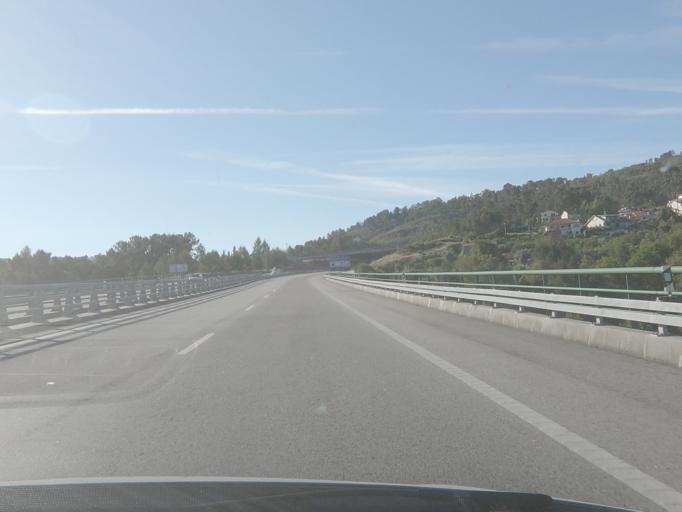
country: PT
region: Viseu
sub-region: Viseu
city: Campo
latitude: 40.8006
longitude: -7.9298
